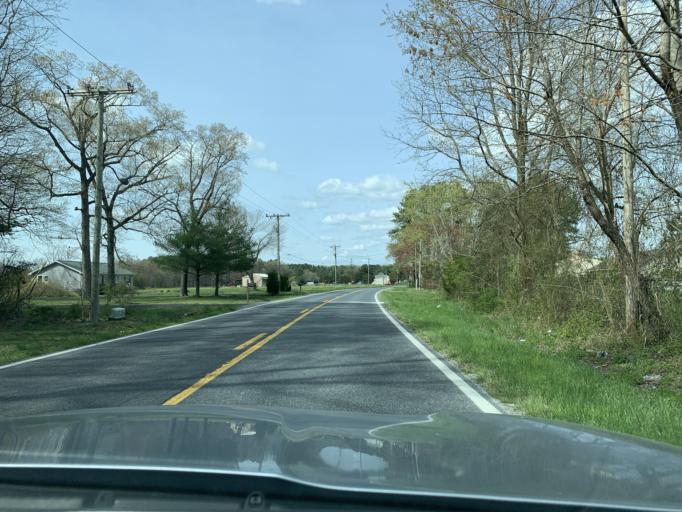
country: US
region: Delaware
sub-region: Sussex County
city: Georgetown
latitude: 38.6362
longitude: -75.3879
